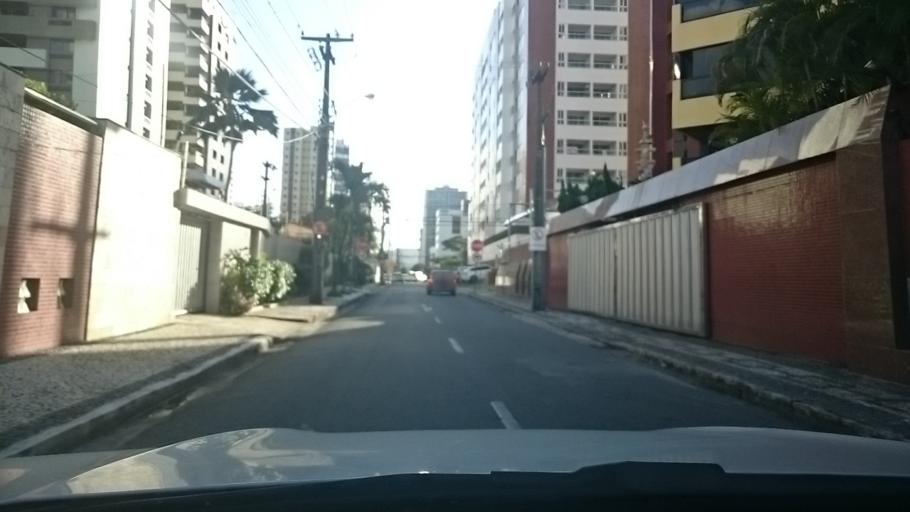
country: BR
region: Paraiba
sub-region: Joao Pessoa
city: Joao Pessoa
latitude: -7.0987
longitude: -34.8376
